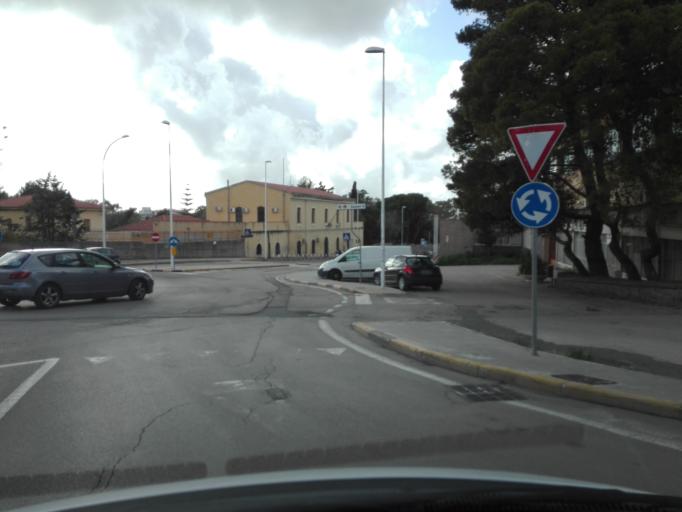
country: IT
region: Sardinia
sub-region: Provincia di Sassari
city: Sassari
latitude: 40.7166
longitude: 8.5763
